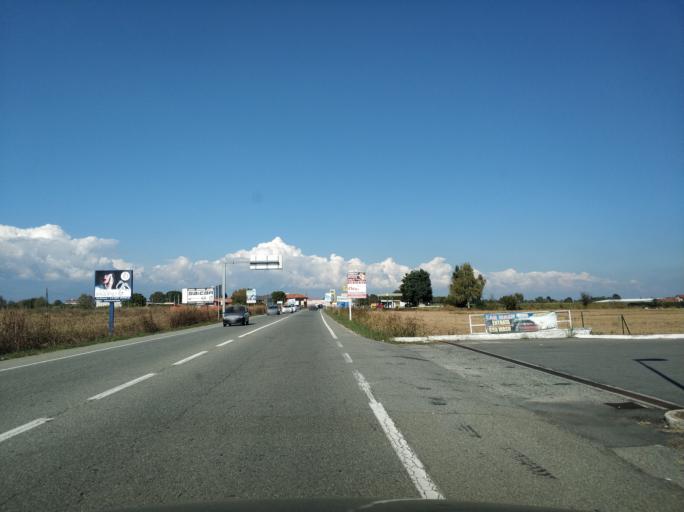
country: IT
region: Piedmont
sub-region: Provincia di Torino
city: Borgaro Torinese
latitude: 45.1607
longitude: 7.6549
